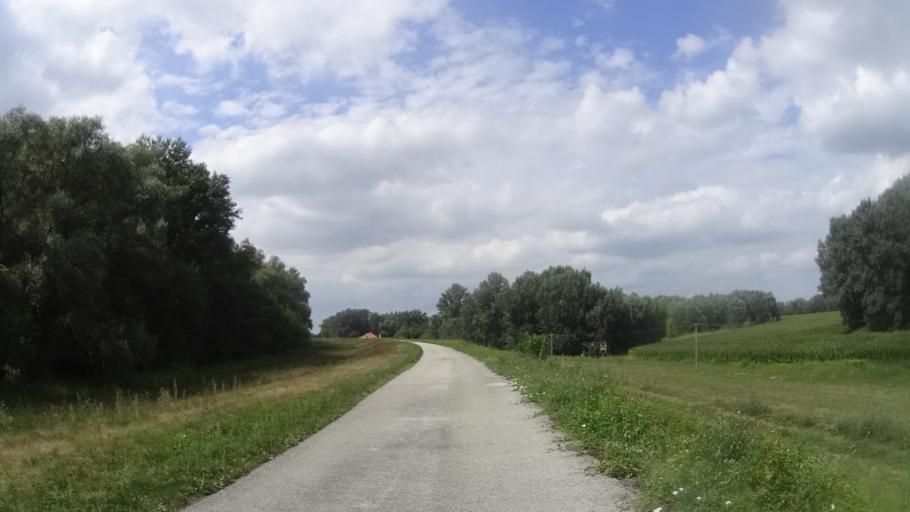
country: SK
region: Trnavsky
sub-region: Okres Dunajska Streda
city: Velky Meder
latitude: 47.7895
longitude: 17.6920
